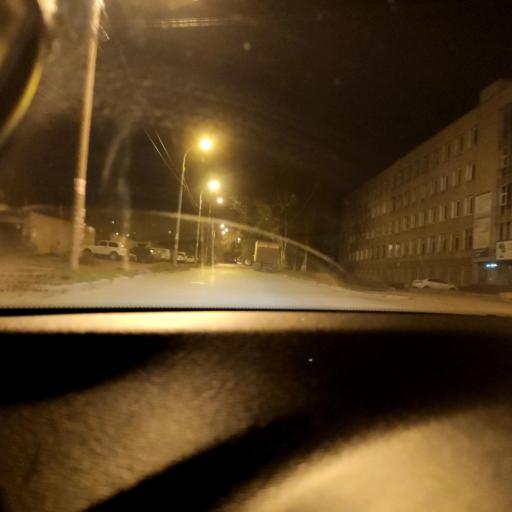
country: RU
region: Samara
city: Samara
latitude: 53.2154
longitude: 50.2305
